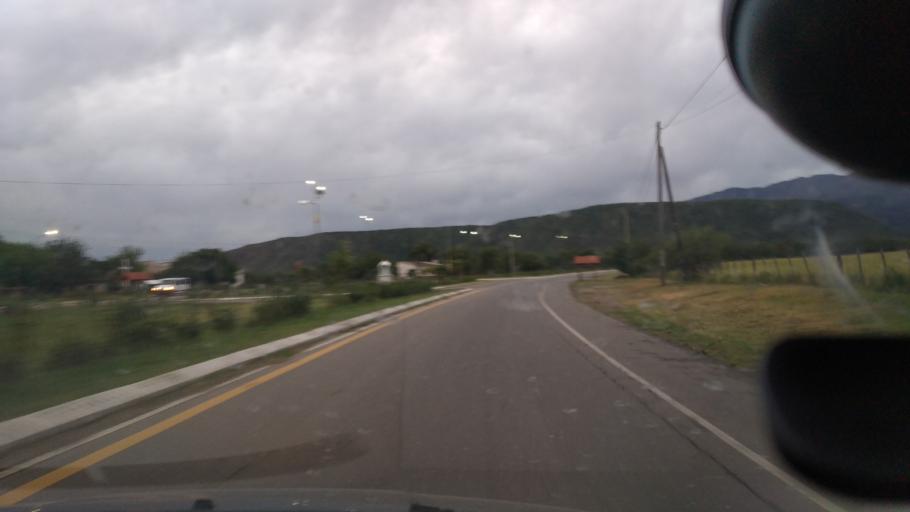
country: AR
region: Cordoba
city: Villa Las Rosas
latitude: -31.9128
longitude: -65.0349
